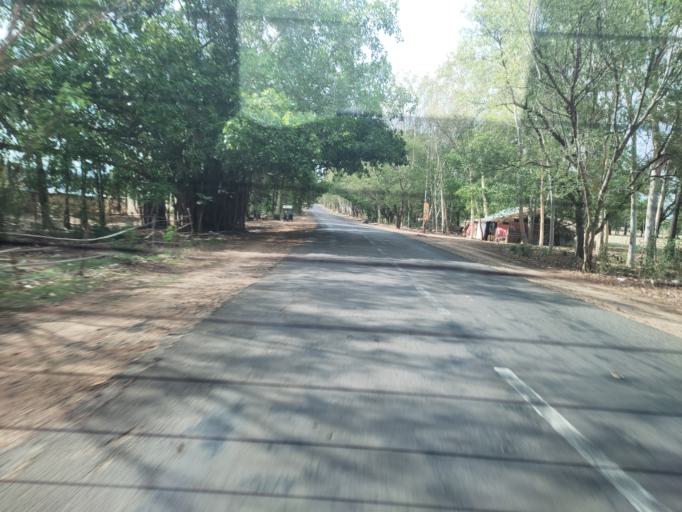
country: MM
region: Magway
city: Magway
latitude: 20.2277
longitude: 95.0184
